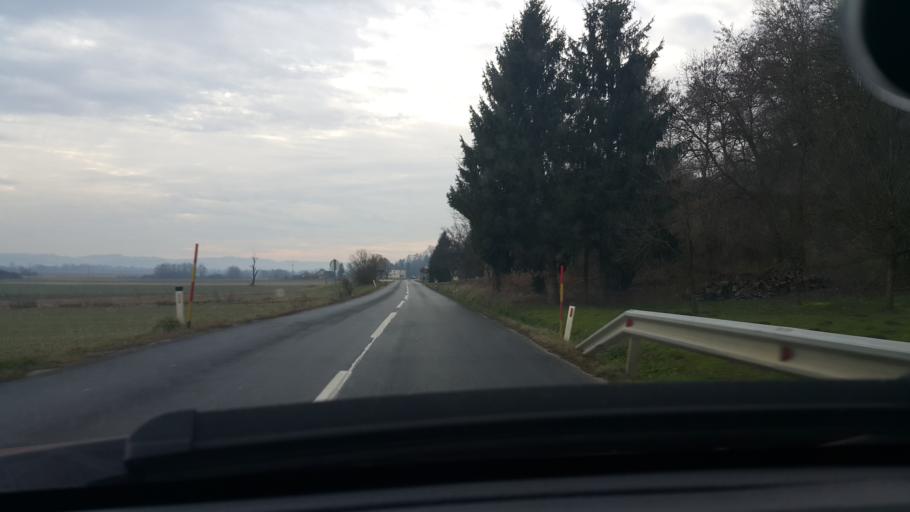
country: SI
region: Bistrica ob Sotli
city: Bistrica ob Sotli
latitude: 45.9865
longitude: 15.6972
